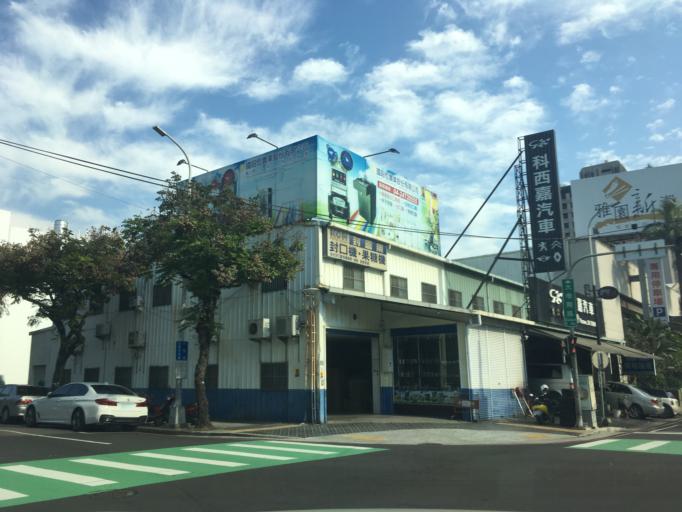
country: TW
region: Taiwan
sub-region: Taichung City
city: Taichung
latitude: 24.1321
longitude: 120.6500
